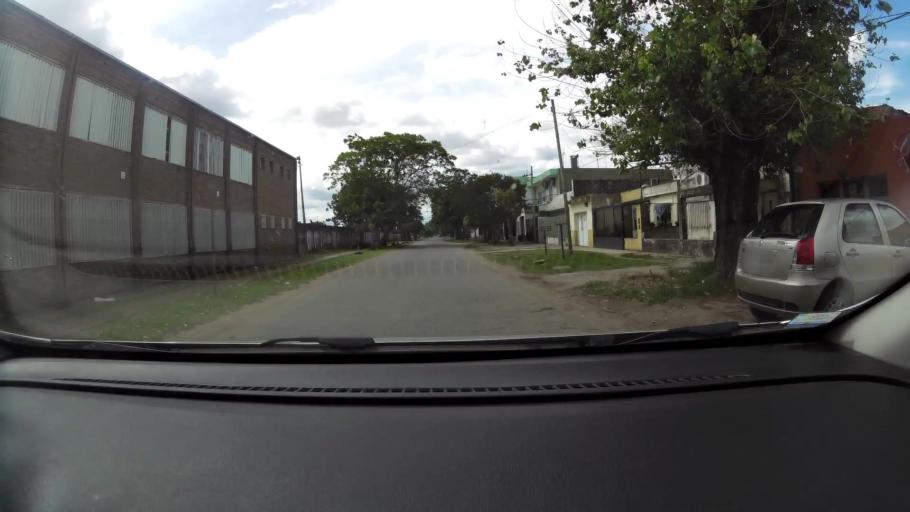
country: AR
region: Santa Fe
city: Gobernador Galvez
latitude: -33.0102
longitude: -60.6446
